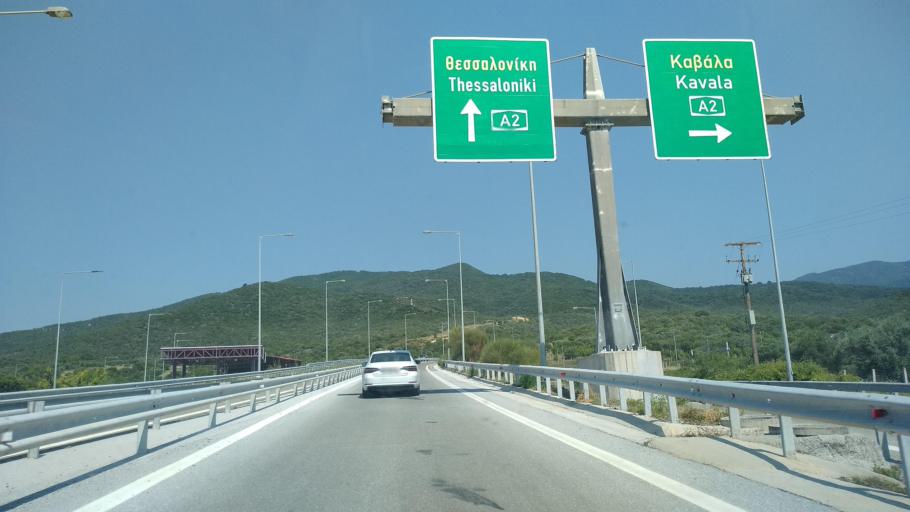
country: GR
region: Central Macedonia
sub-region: Nomos Thessalonikis
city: Nea Vrasna
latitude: 40.7091
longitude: 23.6839
